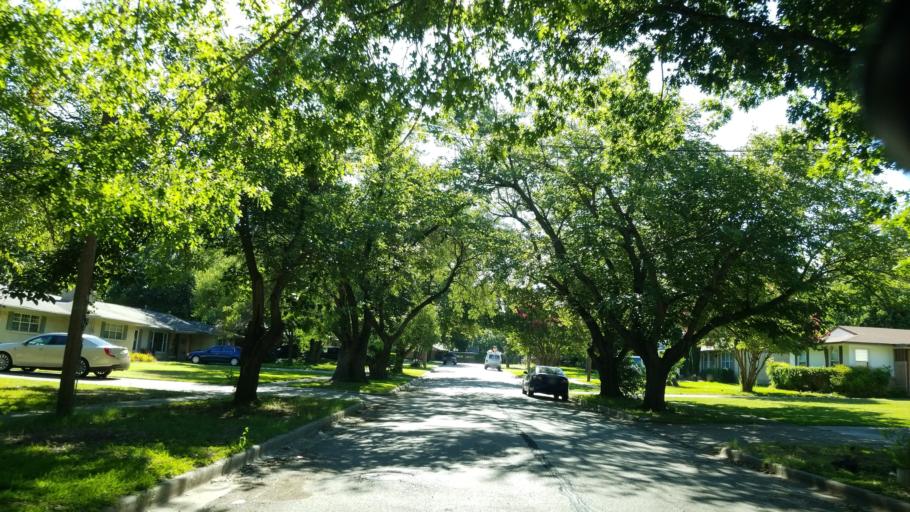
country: US
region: Texas
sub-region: Dallas County
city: Carrollton
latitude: 32.9506
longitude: -96.8961
